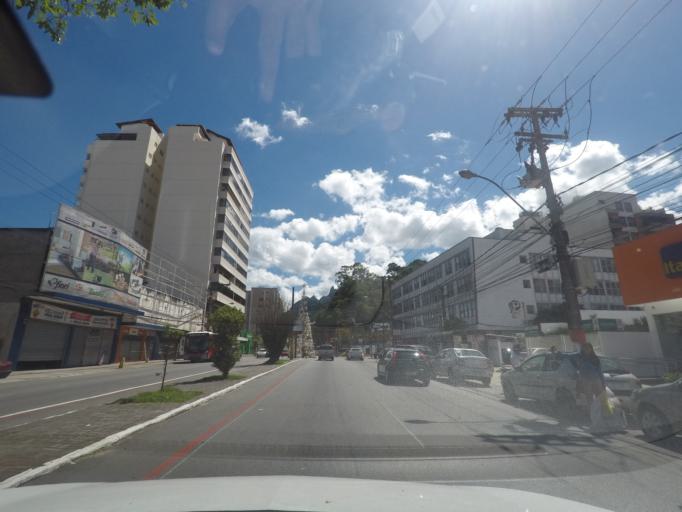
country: BR
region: Rio de Janeiro
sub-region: Teresopolis
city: Teresopolis
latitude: -22.4225
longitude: -42.9768
